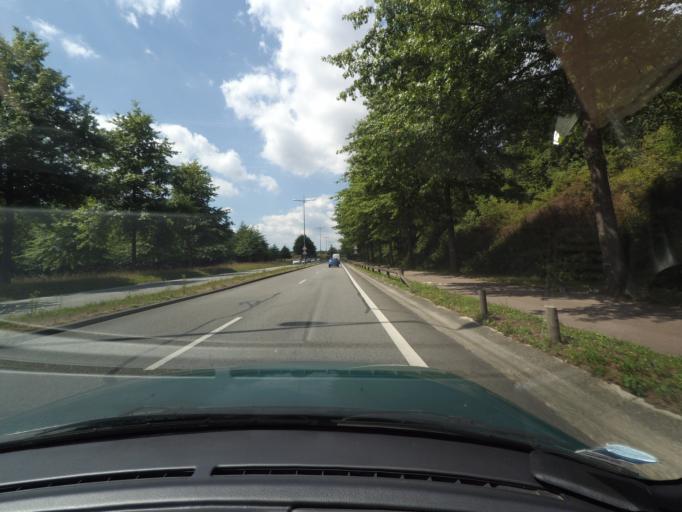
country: FR
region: Limousin
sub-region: Departement de la Haute-Vienne
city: Condat-sur-Vienne
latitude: 45.8037
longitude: 1.2820
